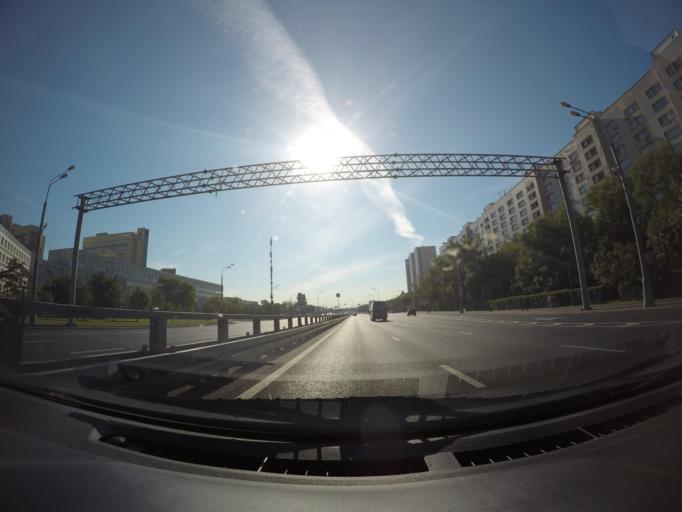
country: RU
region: Moscow
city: Vykhino-Zhulebino
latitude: 55.7134
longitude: 37.8117
